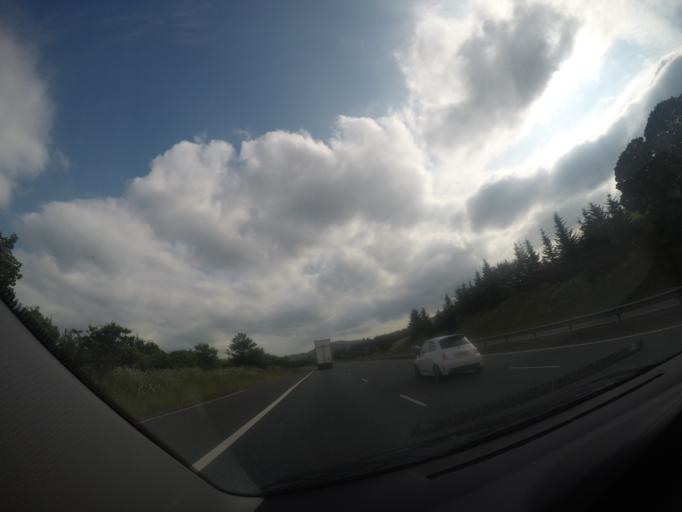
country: GB
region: Scotland
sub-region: South Lanarkshire
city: Douglas
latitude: 55.4968
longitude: -3.6945
